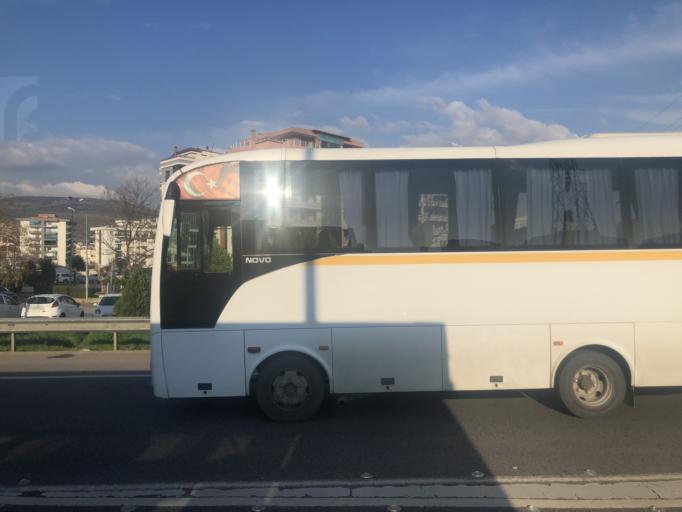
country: TR
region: Izmir
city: Karsiyaka
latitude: 38.4848
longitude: 27.0623
